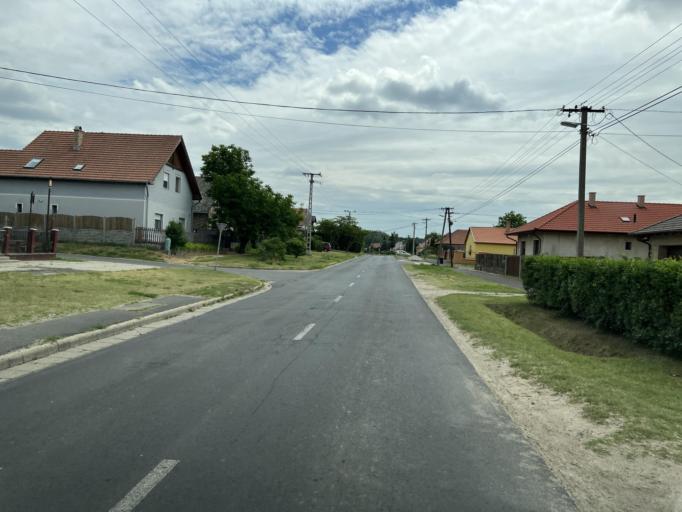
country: HU
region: Pest
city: Koka
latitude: 47.4827
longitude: 19.5959
